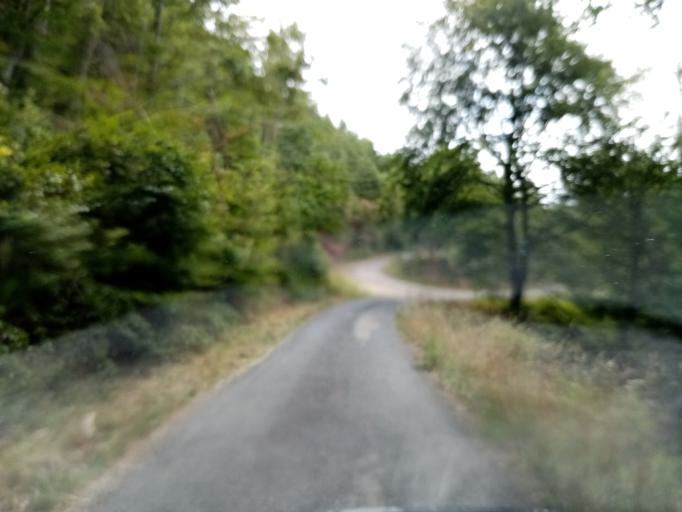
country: FR
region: Alsace
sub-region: Departement du Bas-Rhin
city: Ville
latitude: 48.3531
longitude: 7.3622
